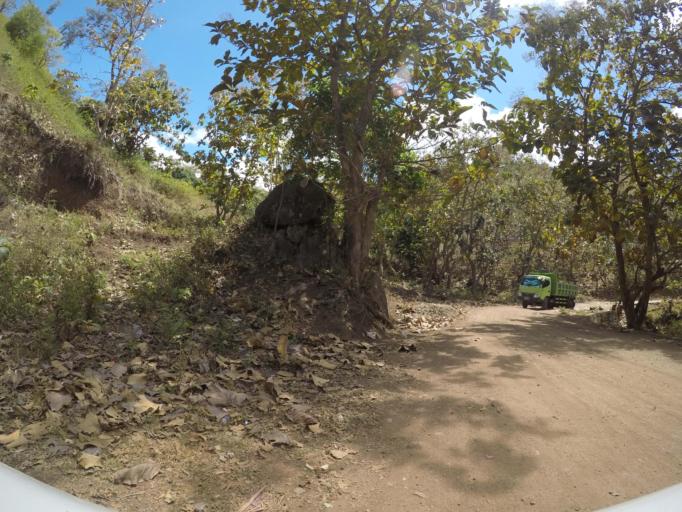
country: TL
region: Lautem
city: Lospalos
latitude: -8.5417
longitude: 126.8282
